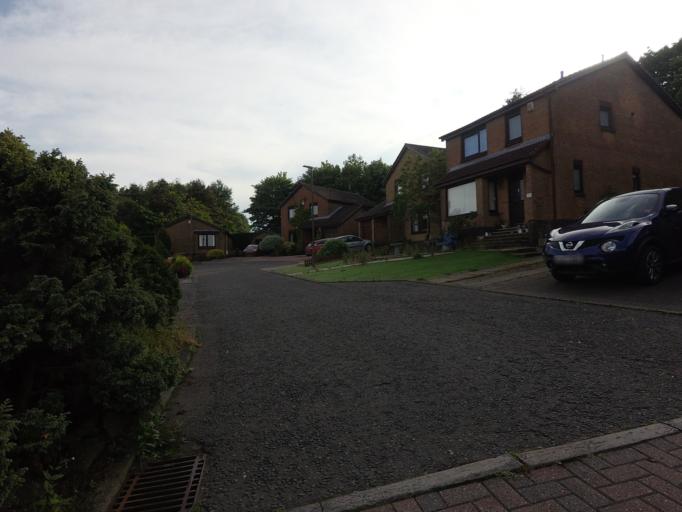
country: GB
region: Scotland
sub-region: West Lothian
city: Livingston
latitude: 55.9106
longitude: -3.5426
